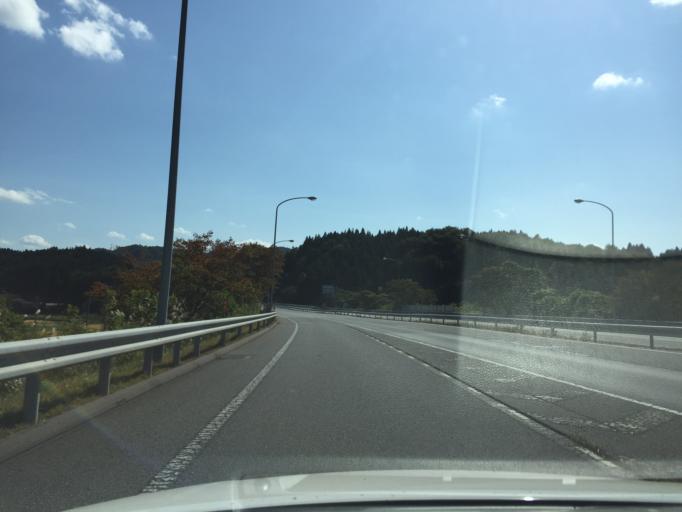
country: JP
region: Fukushima
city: Funehikimachi-funehiki
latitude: 37.2888
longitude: 140.6129
